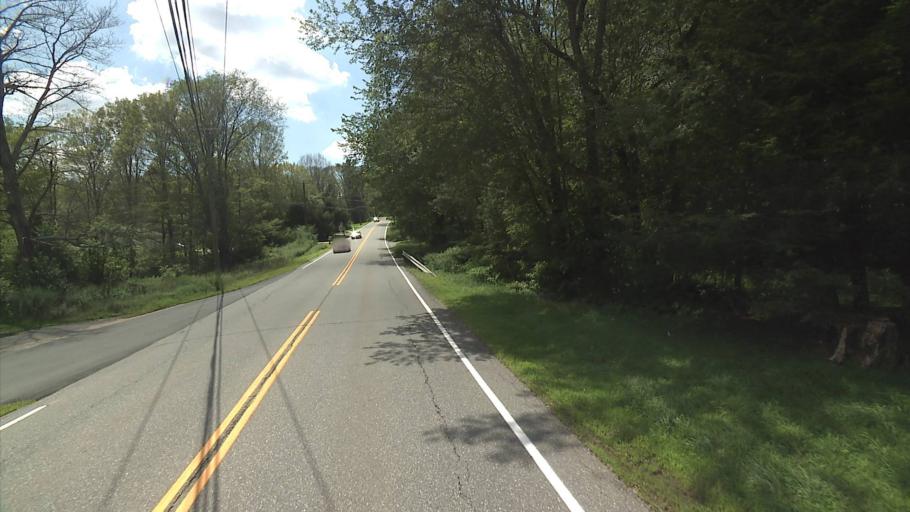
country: US
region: Connecticut
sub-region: Windham County
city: Windham
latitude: 41.7904
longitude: -72.1274
